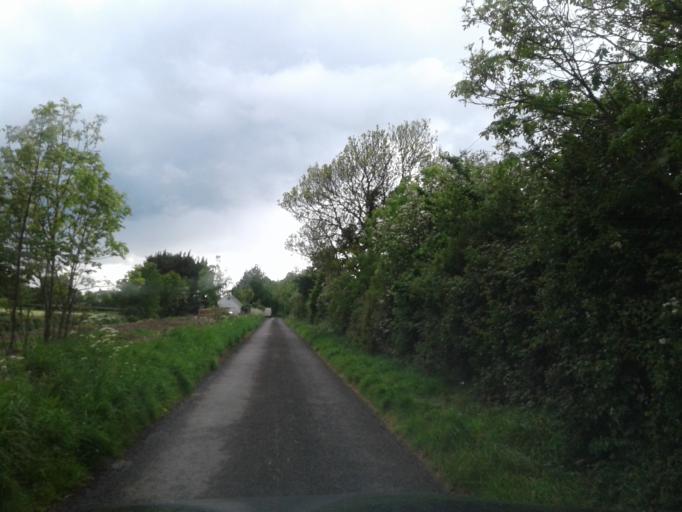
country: IE
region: Leinster
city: Ballymun
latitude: 53.4259
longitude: -6.2753
